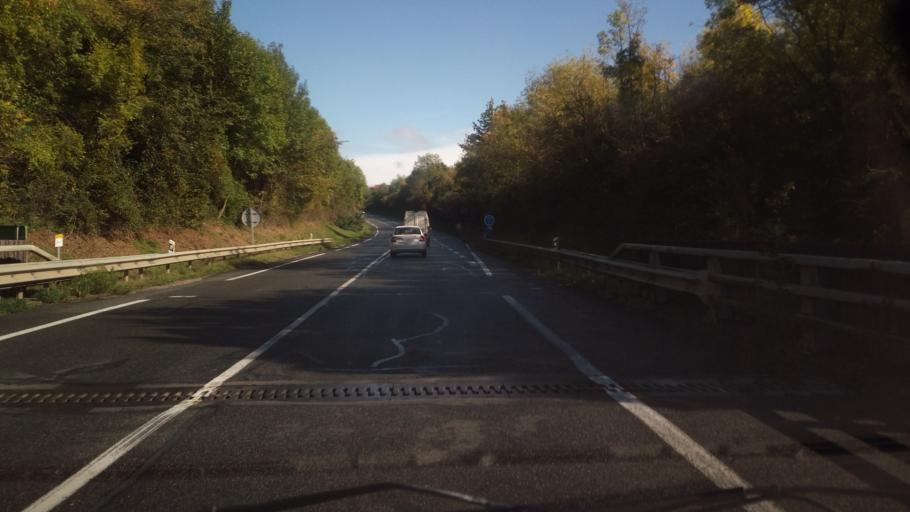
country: FR
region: Centre
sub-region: Departement du Loiret
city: Gien
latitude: 47.6792
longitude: 2.6455
